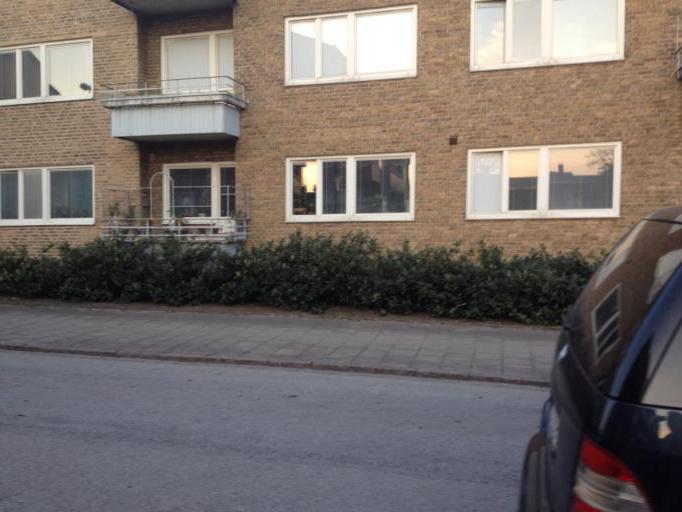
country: SE
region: Skane
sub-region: Burlovs Kommun
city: Arloev
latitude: 55.6081
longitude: 13.0447
